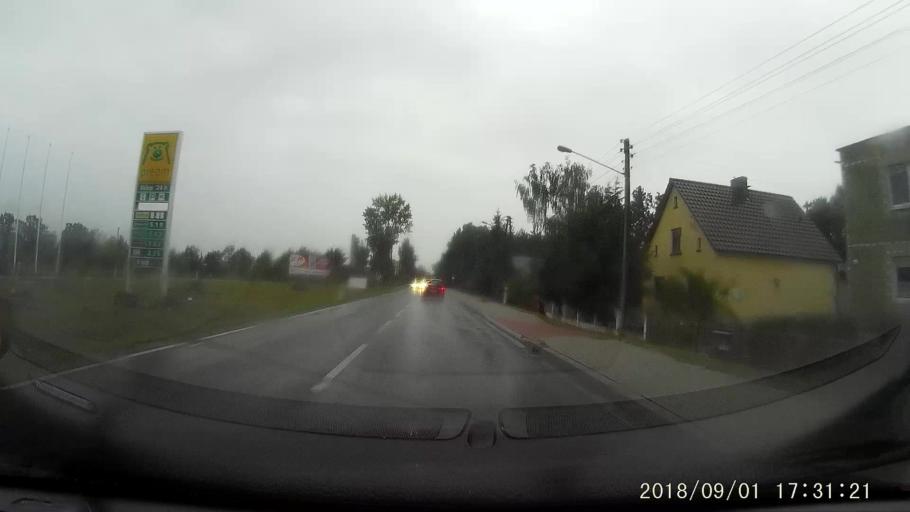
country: PL
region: Lubusz
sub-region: Powiat zaganski
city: Zagan
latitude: 51.6338
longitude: 15.3246
